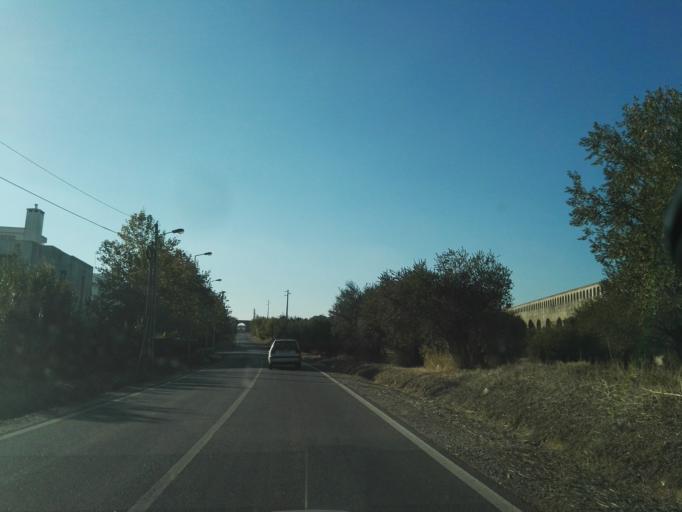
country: PT
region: Portalegre
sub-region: Elvas
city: Elvas
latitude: 38.8785
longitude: -7.1787
